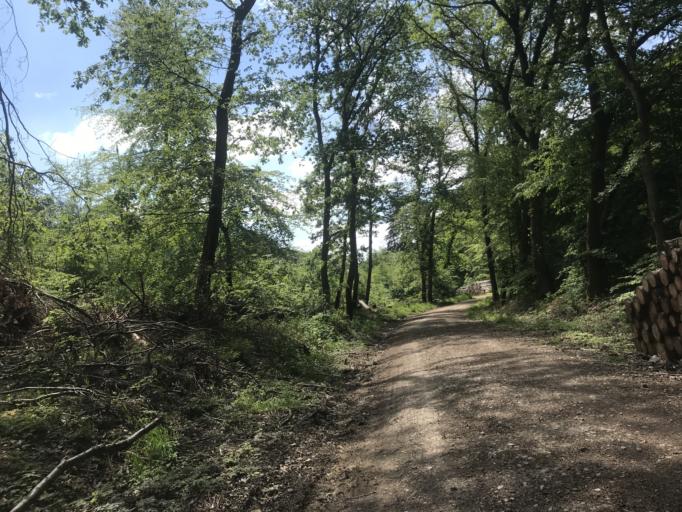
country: DE
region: Hesse
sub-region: Regierungsbezirk Darmstadt
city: Walluf
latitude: 50.0841
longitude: 8.1452
